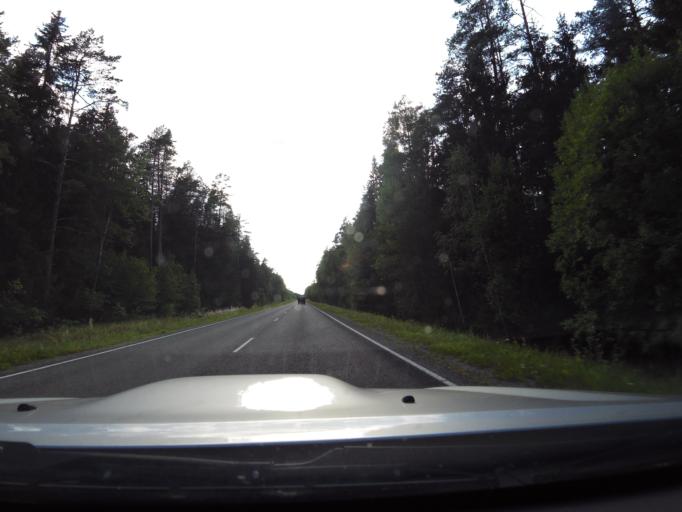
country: LT
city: Juodupe
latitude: 56.2040
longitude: 25.5870
